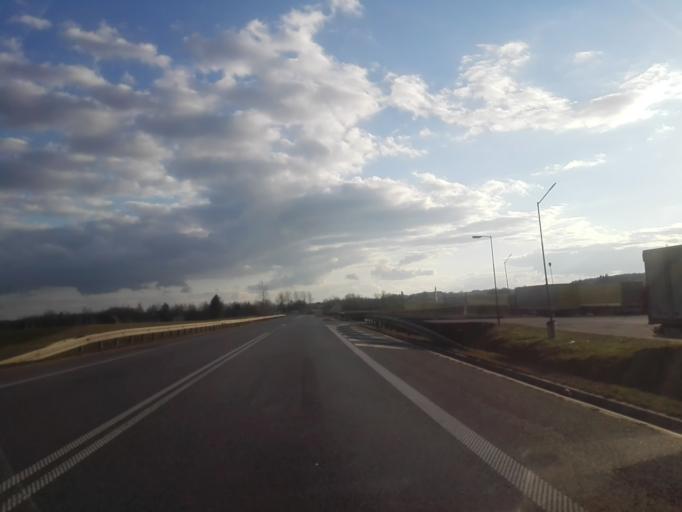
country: PL
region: Podlasie
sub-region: Suwalki
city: Suwalki
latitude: 54.1776
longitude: 22.9970
